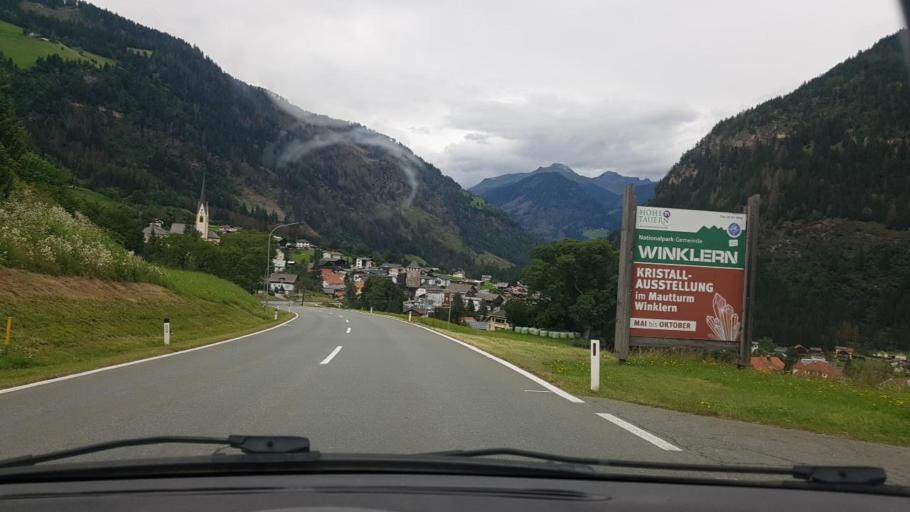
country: AT
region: Carinthia
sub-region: Politischer Bezirk Spittal an der Drau
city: Winklern
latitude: 46.8659
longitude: 12.8754
